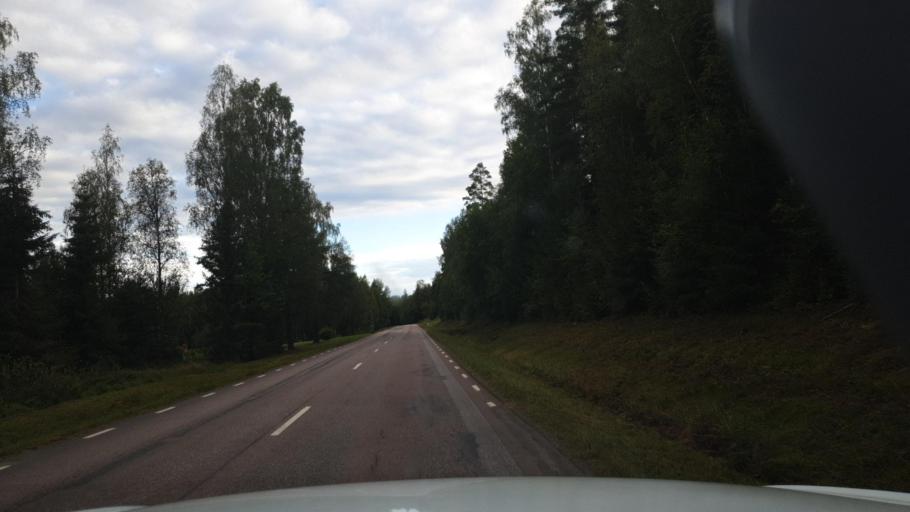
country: SE
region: Vaermland
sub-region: Eda Kommun
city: Charlottenberg
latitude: 59.8986
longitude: 12.3007
